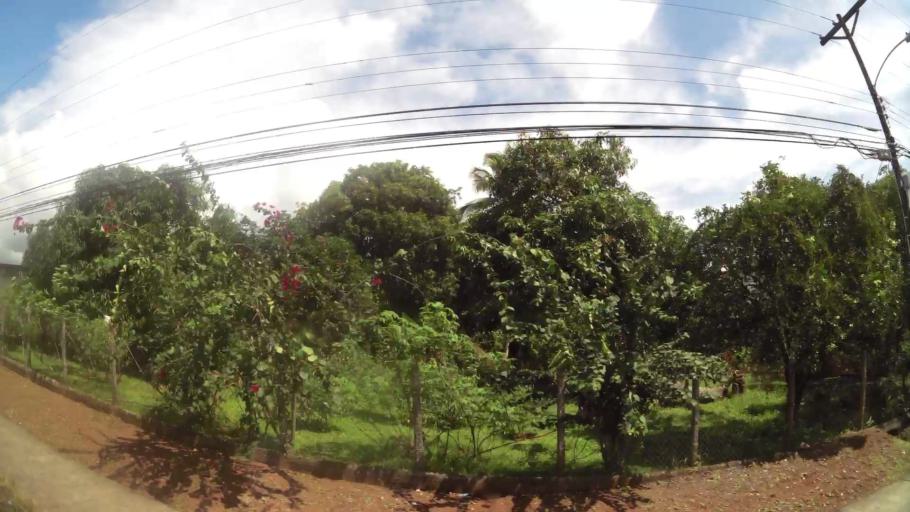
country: PA
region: Panama
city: Vista Alegre
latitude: 8.9291
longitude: -79.7015
